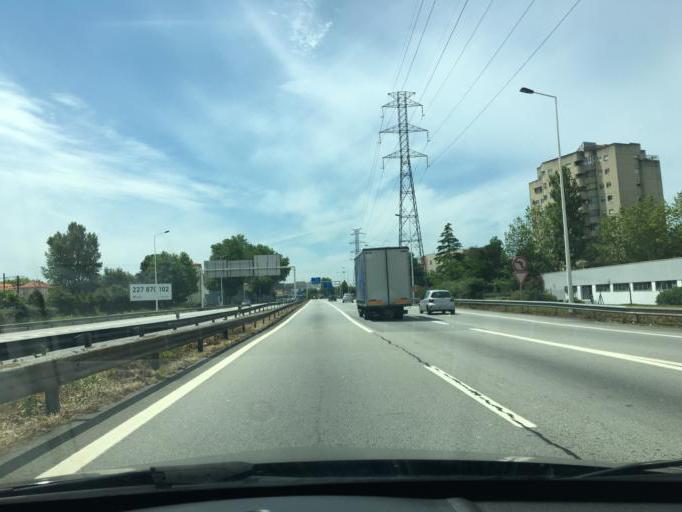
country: PT
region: Porto
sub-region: Matosinhos
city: Sao Mamede de Infesta
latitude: 41.1783
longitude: -8.6225
